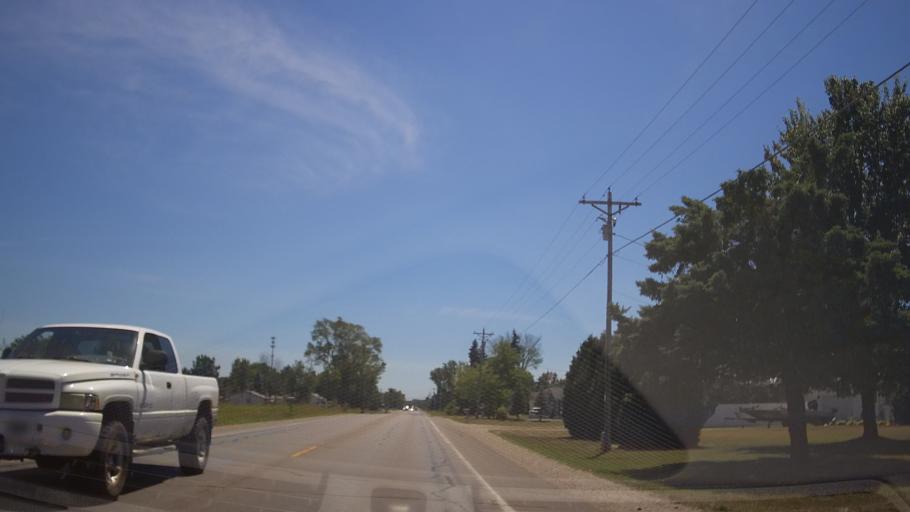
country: US
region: Michigan
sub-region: Grand Traverse County
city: Traverse City
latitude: 44.6770
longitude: -85.6898
